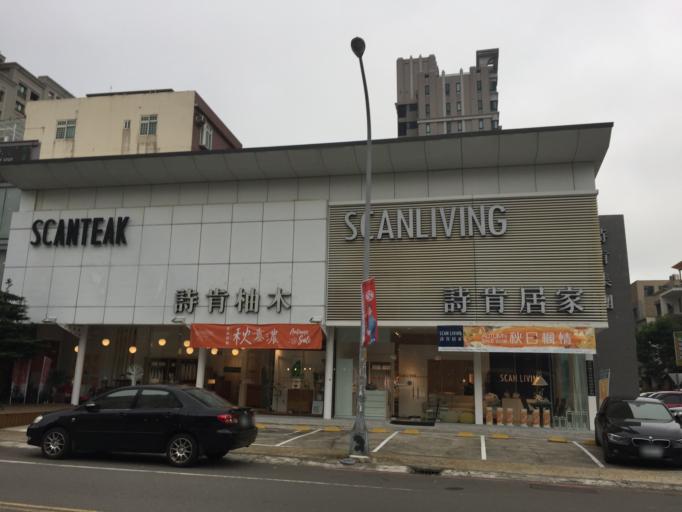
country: TW
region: Taiwan
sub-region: Hsinchu
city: Zhubei
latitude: 24.8200
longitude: 121.0240
